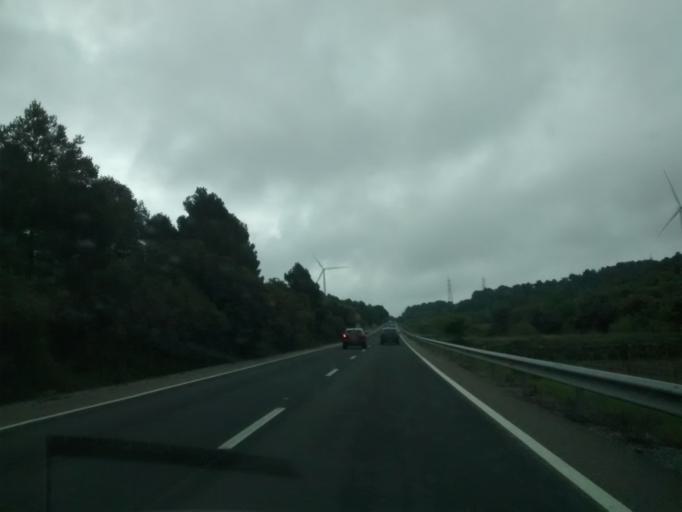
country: ES
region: Catalonia
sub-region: Provincia de Tarragona
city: Batea
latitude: 41.0618
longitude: 0.3499
